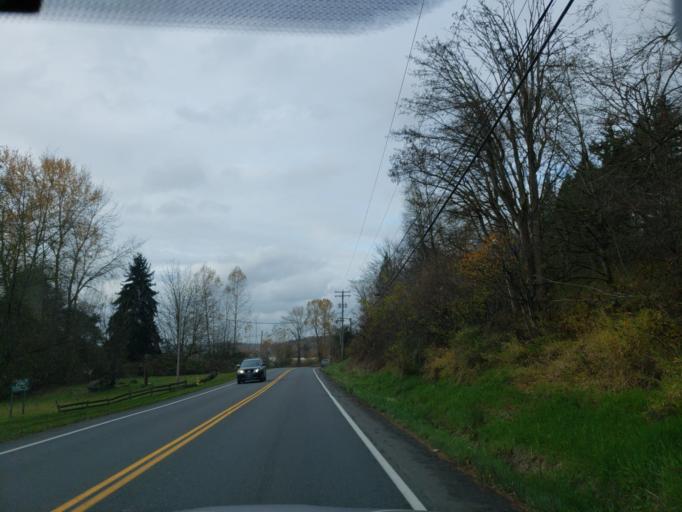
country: US
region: Washington
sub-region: King County
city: Woodinville
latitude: 47.7412
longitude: -122.1447
